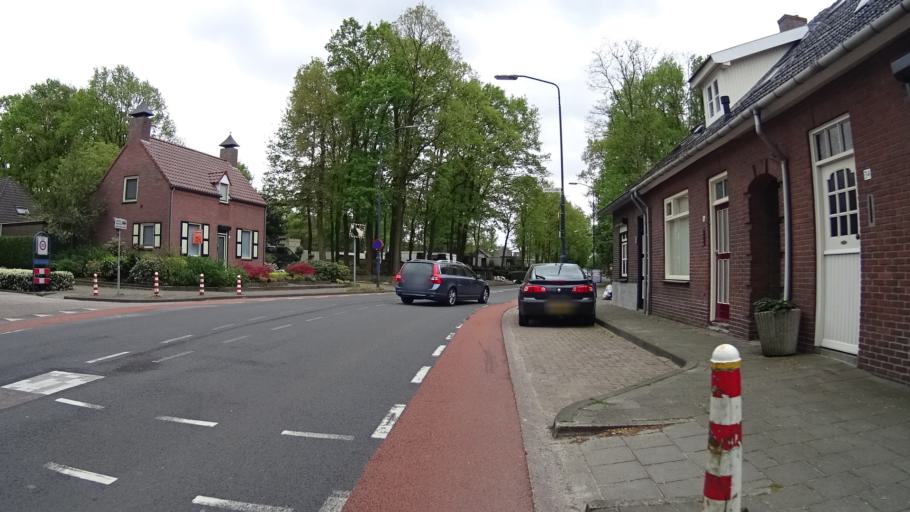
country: NL
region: North Brabant
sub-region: Gemeente Boekel
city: Boekel
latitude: 51.5992
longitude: 5.6766
